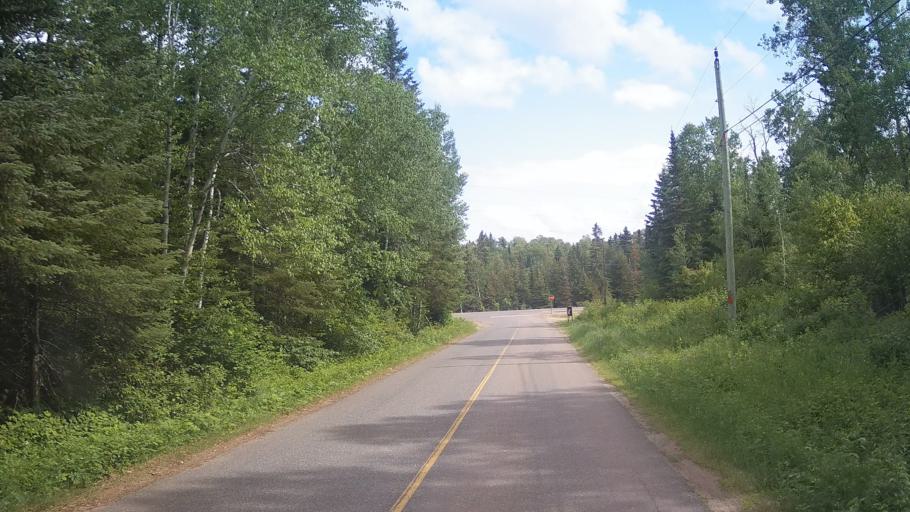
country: CA
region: Ontario
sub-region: Thunder Bay District
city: Thunder Bay
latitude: 48.6639
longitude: -88.6613
